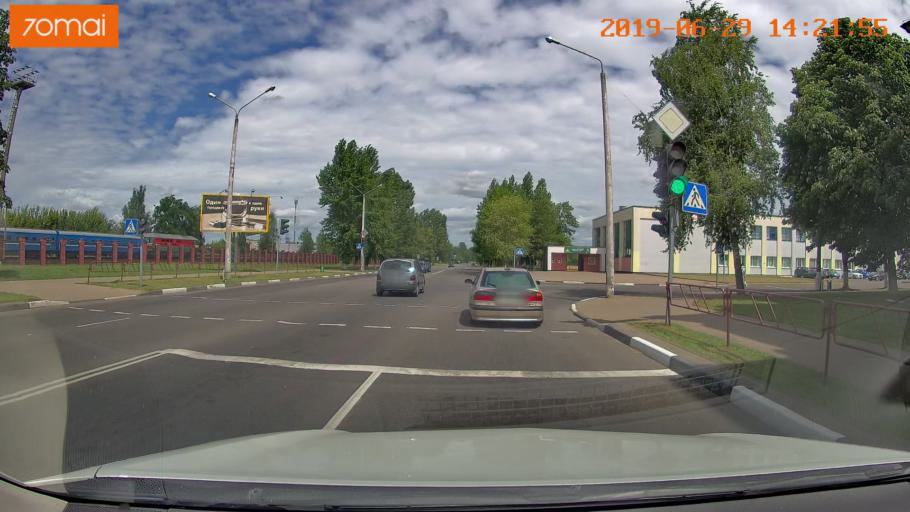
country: BY
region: Minsk
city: Salihorsk
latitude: 52.7935
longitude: 27.5481
